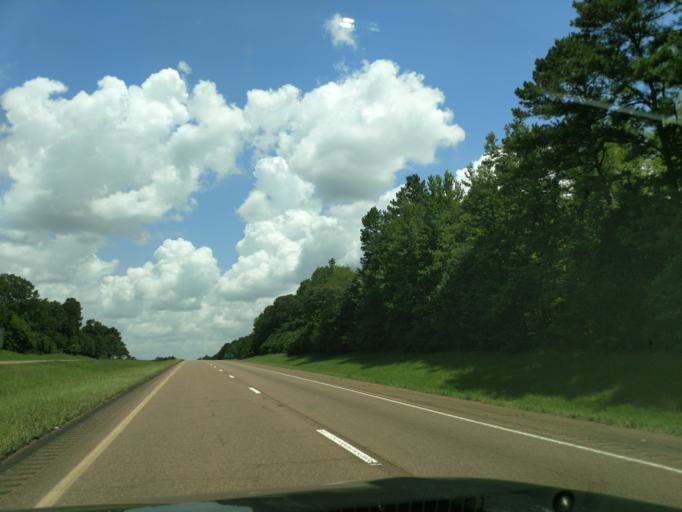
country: US
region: Mississippi
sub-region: Montgomery County
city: Winona
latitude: 33.5007
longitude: -89.7652
